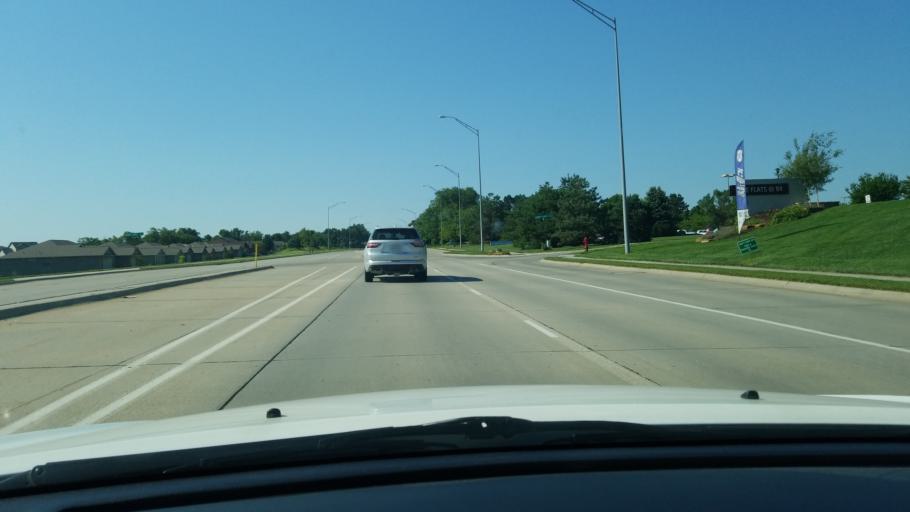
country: US
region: Nebraska
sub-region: Lancaster County
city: Lincoln
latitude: 40.7506
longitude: -96.6062
